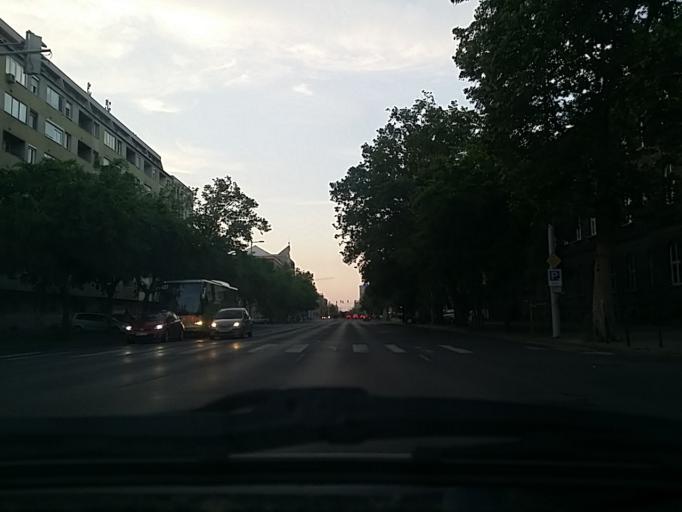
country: HU
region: Budapest
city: Budapest VI. keruelet
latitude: 47.5220
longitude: 19.0622
